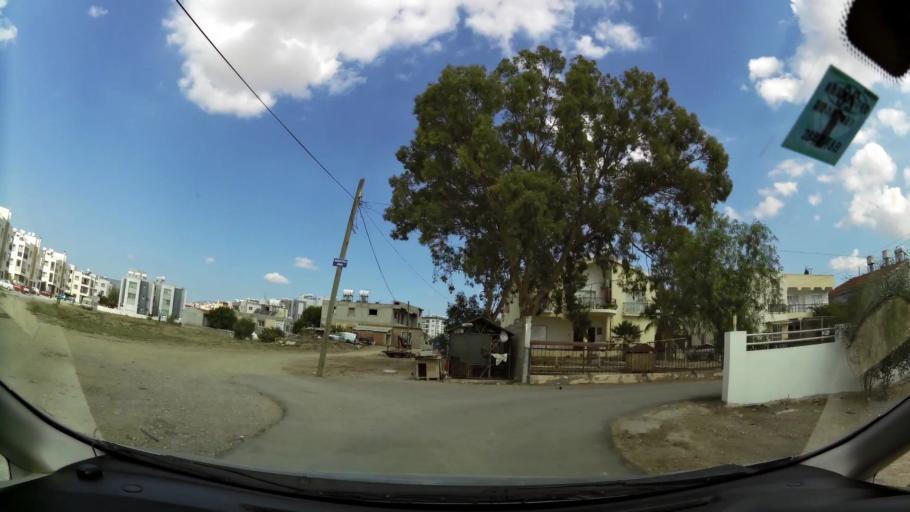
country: CY
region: Lefkosia
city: Nicosia
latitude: 35.2179
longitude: 33.3012
